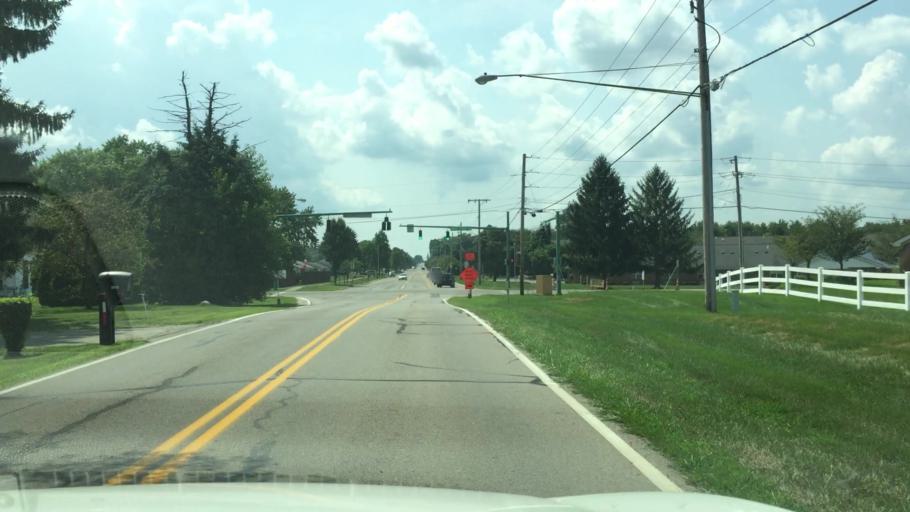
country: US
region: Ohio
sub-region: Clark County
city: Northridge
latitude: 39.9656
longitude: -83.7651
